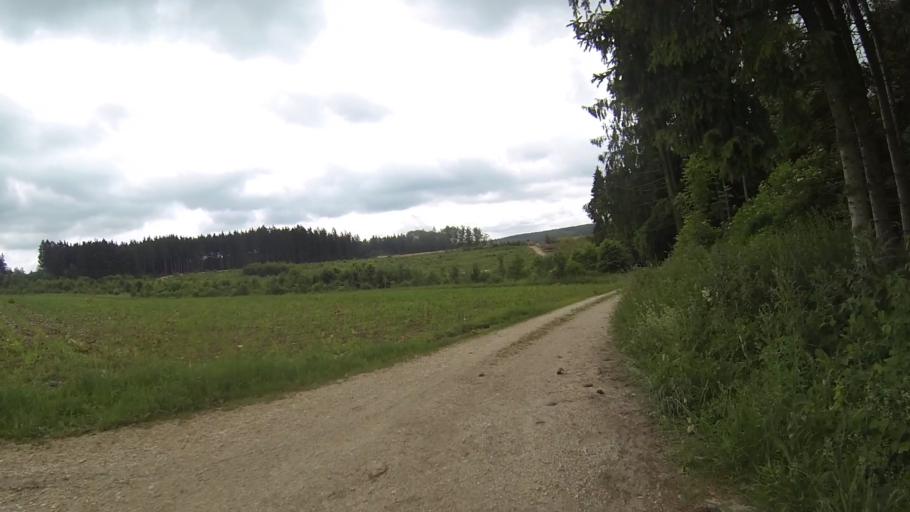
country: DE
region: Baden-Wuerttemberg
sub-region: Regierungsbezirk Stuttgart
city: Gerstetten
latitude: 48.6764
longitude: 10.0179
